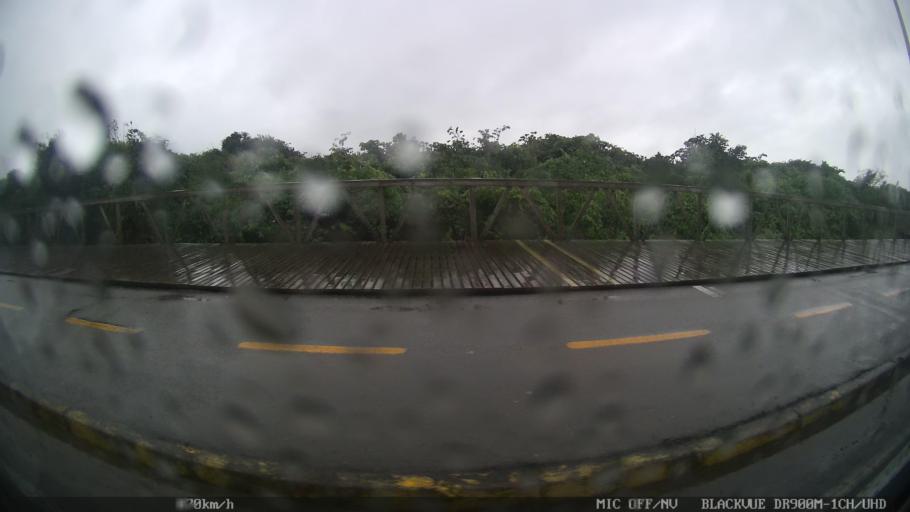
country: BR
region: Santa Catarina
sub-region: Navegantes
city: Navegantes
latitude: -26.8839
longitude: -48.6415
